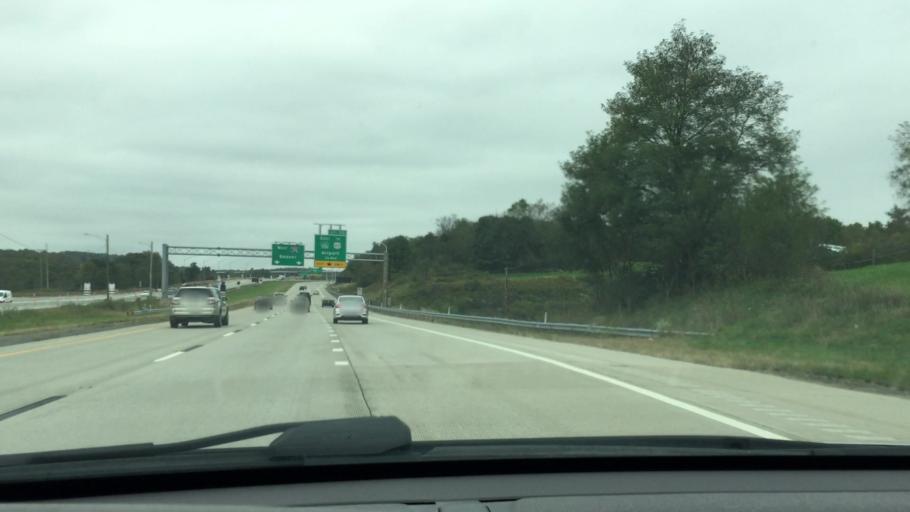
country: US
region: Pennsylvania
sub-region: Allegheny County
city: Imperial
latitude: 40.4793
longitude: -80.2557
